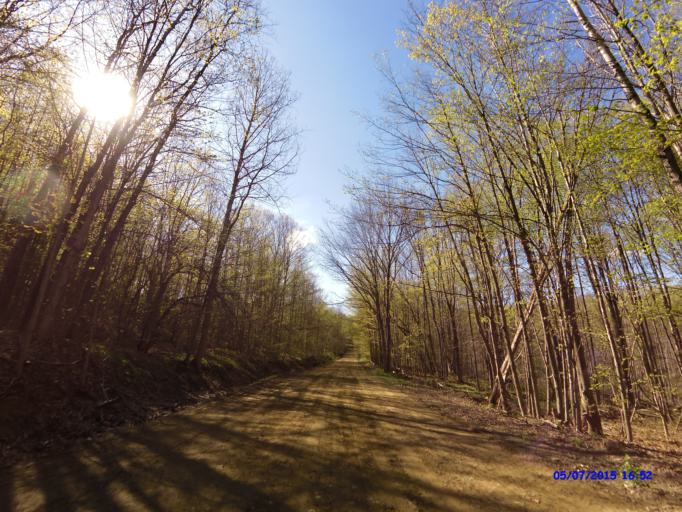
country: US
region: New York
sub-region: Cattaraugus County
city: Little Valley
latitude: 42.2879
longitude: -78.7250
